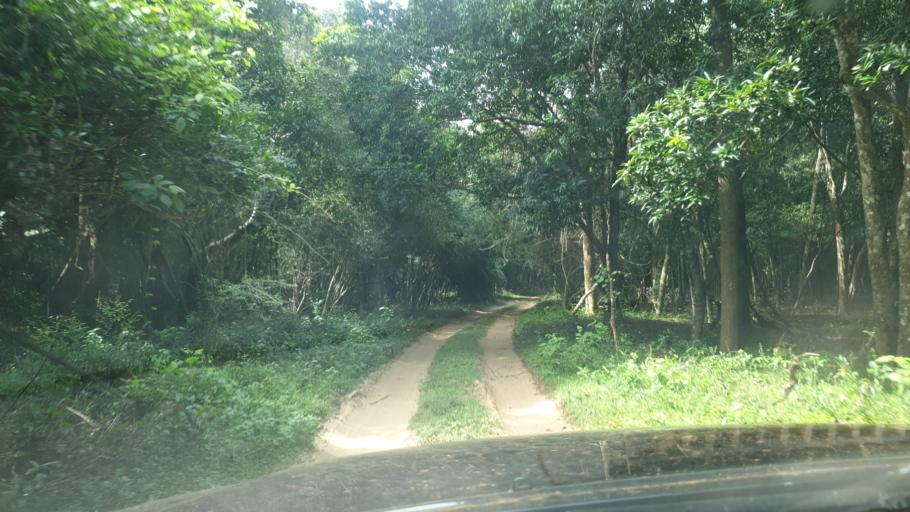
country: LK
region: North Western
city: Puttalam
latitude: 8.4115
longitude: 79.9857
